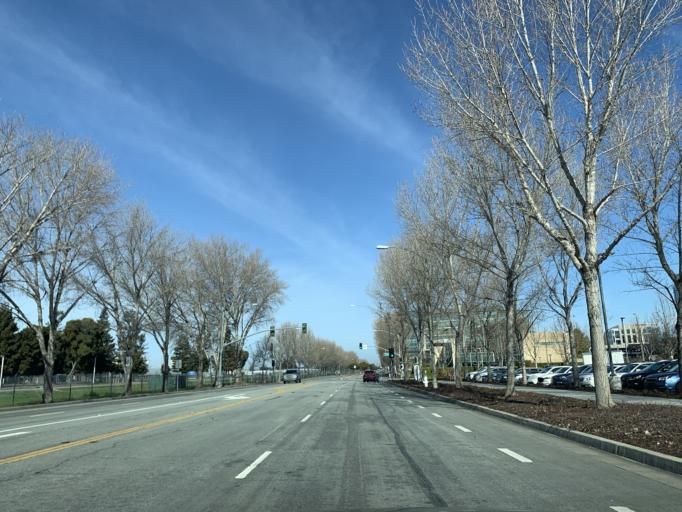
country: US
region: California
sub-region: Santa Clara County
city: Sunnyvale
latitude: 37.4051
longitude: -122.0370
